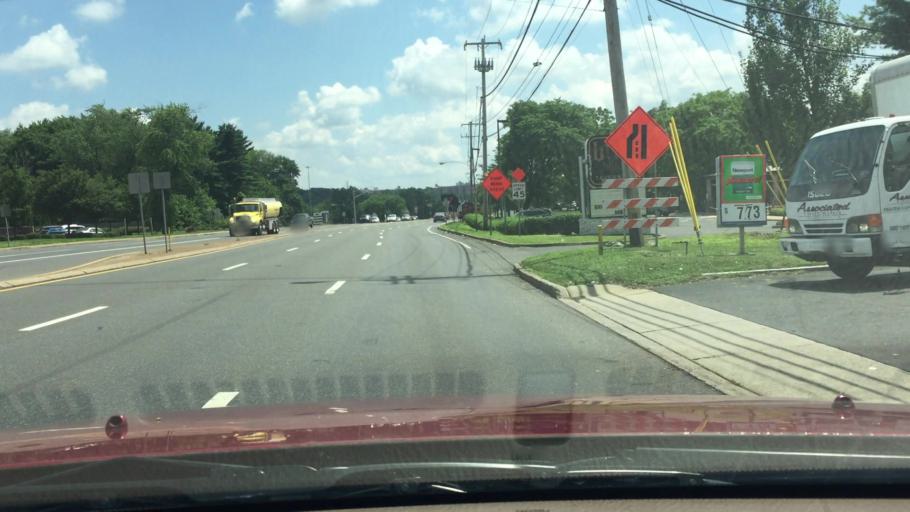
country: US
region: Pennsylvania
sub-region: Montgomery County
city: Horsham
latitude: 40.1680
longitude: -75.1261
